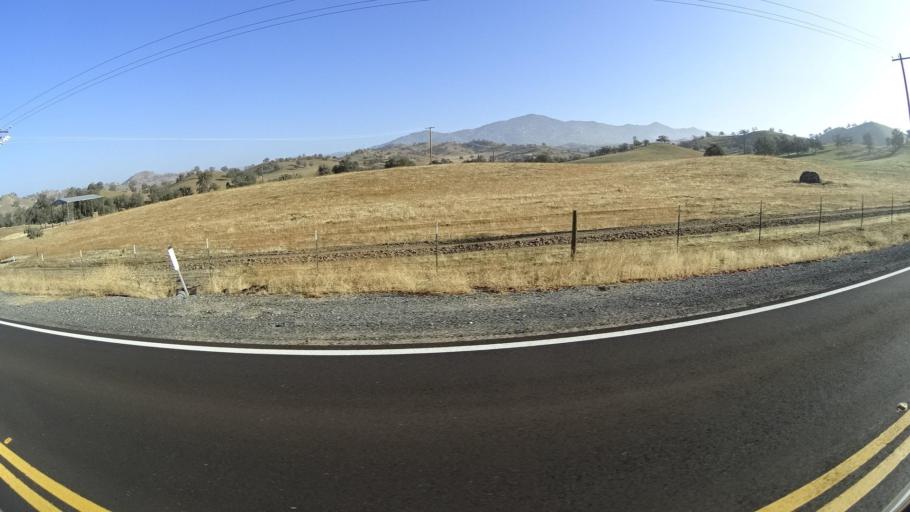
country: US
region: California
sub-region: Tulare County
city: Richgrove
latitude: 35.7288
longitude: -118.8577
